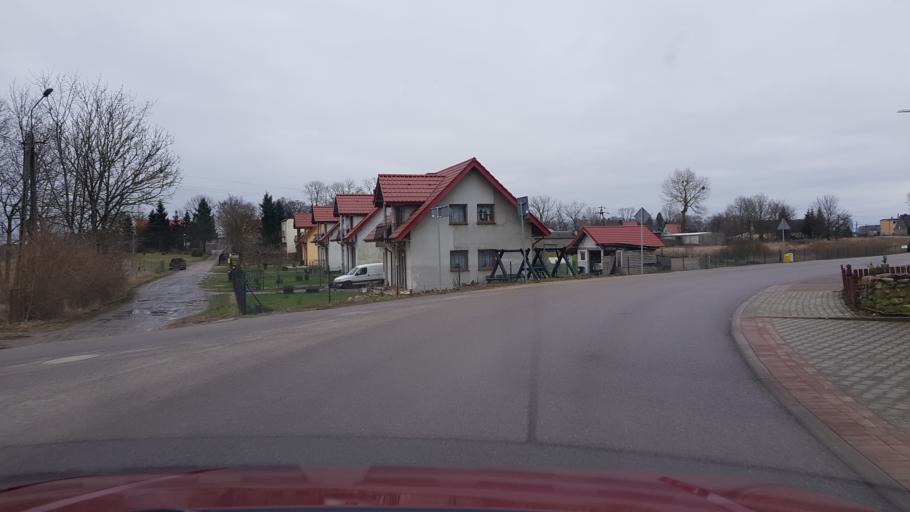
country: PL
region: West Pomeranian Voivodeship
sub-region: Powiat koszalinski
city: Mielno
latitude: 54.1651
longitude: 16.0362
